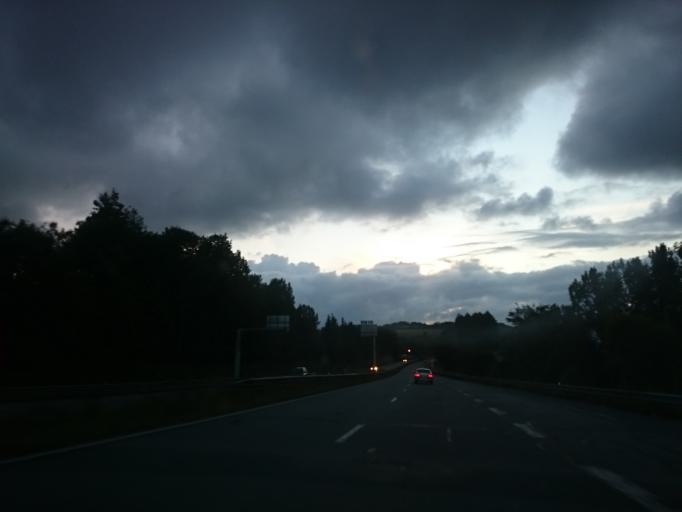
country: FR
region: Brittany
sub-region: Departement du Finistere
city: Ergue-Gaberic
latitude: 48.0025
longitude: -4.0546
